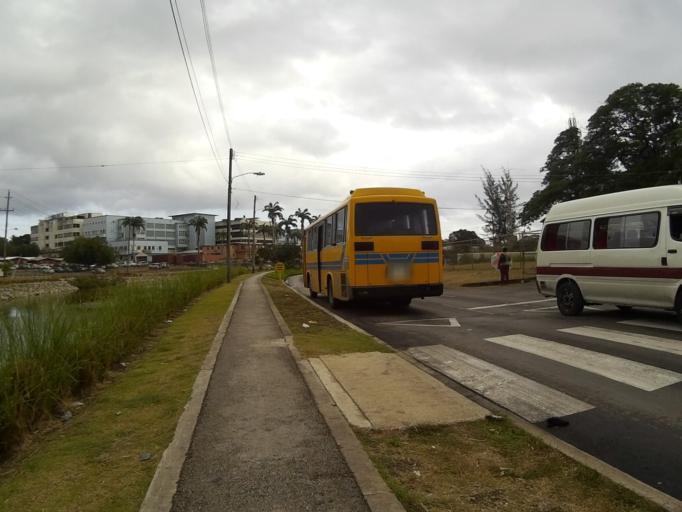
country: BB
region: Saint Michael
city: Bridgetown
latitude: 13.0975
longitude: -59.6077
